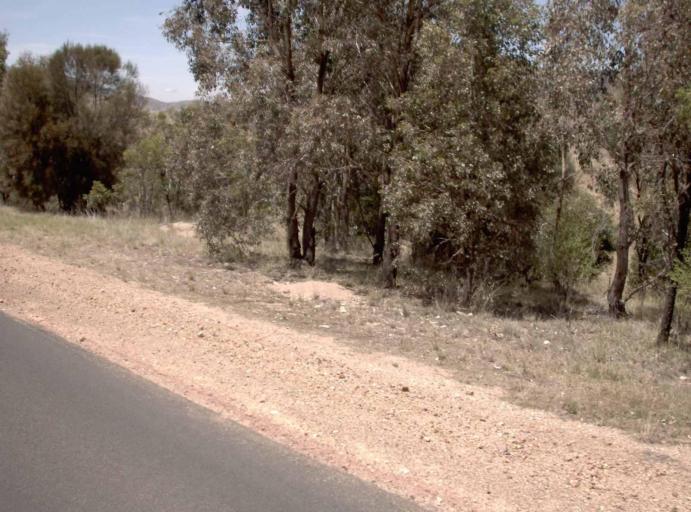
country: AU
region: Victoria
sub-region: East Gippsland
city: Bairnsdale
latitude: -37.1716
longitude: 147.6924
